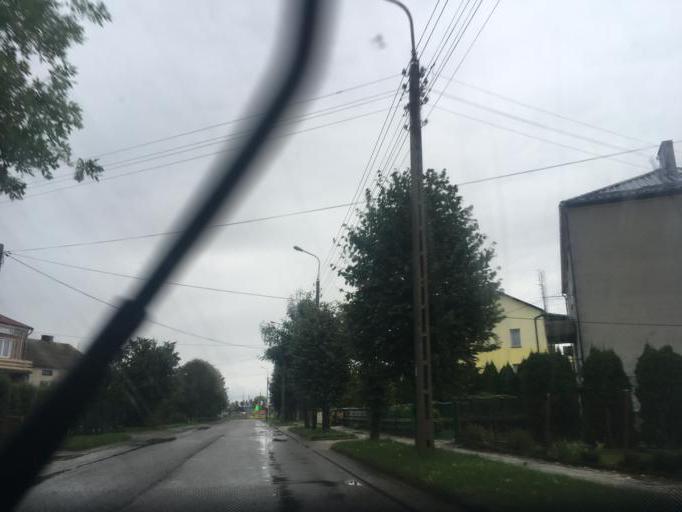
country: PL
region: Podlasie
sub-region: Powiat bielski
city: Bransk
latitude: 52.7454
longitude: 22.8543
